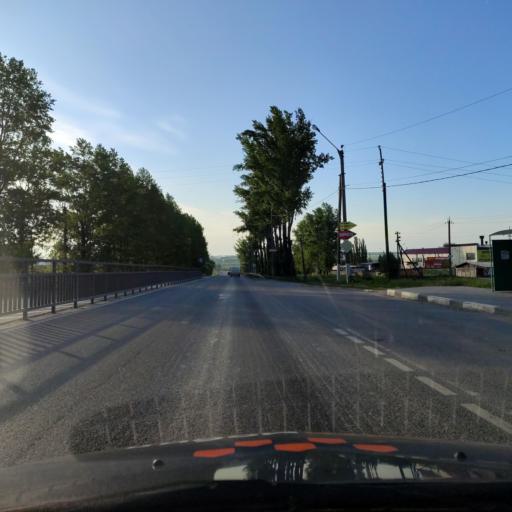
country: RU
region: Lipetsk
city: Yelets
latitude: 52.5943
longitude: 38.4837
